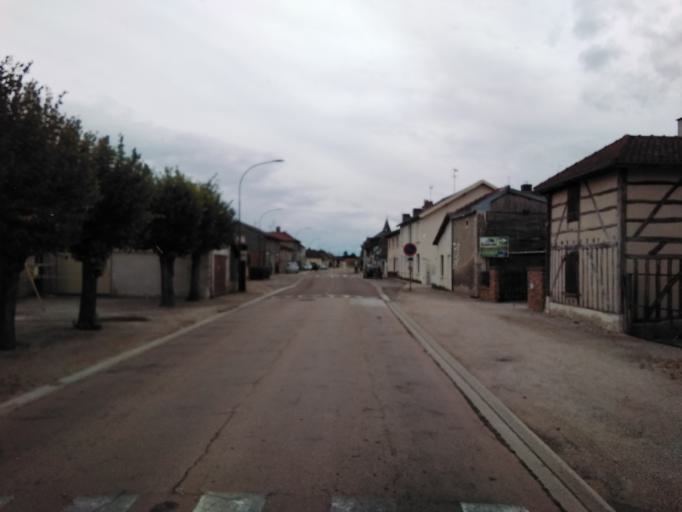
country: FR
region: Champagne-Ardenne
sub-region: Departement de l'Aube
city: Brienne-le-Chateau
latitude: 48.3764
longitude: 4.5296
